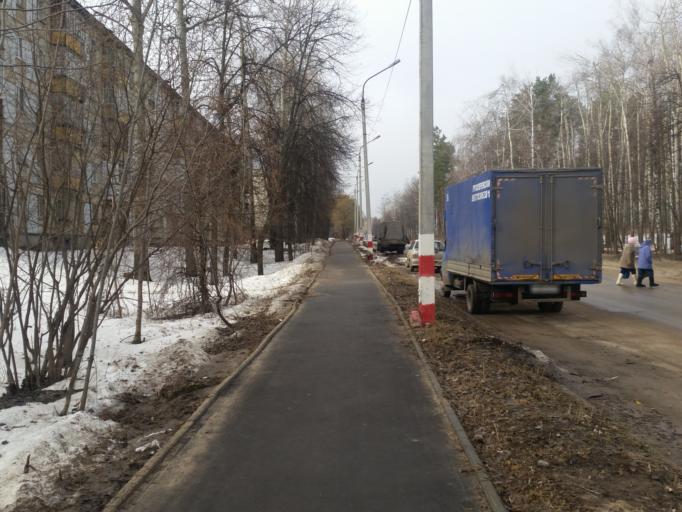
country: RU
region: Ulyanovsk
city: Dimitrovgrad
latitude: 54.2395
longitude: 49.5541
